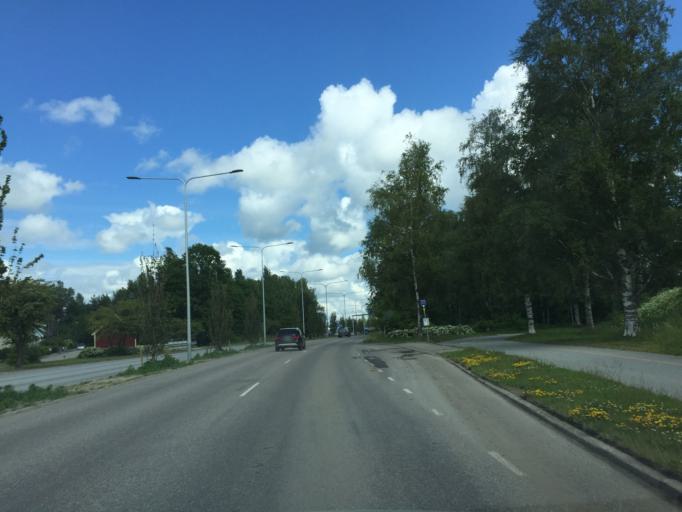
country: SE
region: OErebro
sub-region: Orebro Kommun
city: Orebro
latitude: 59.2927
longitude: 15.2262
